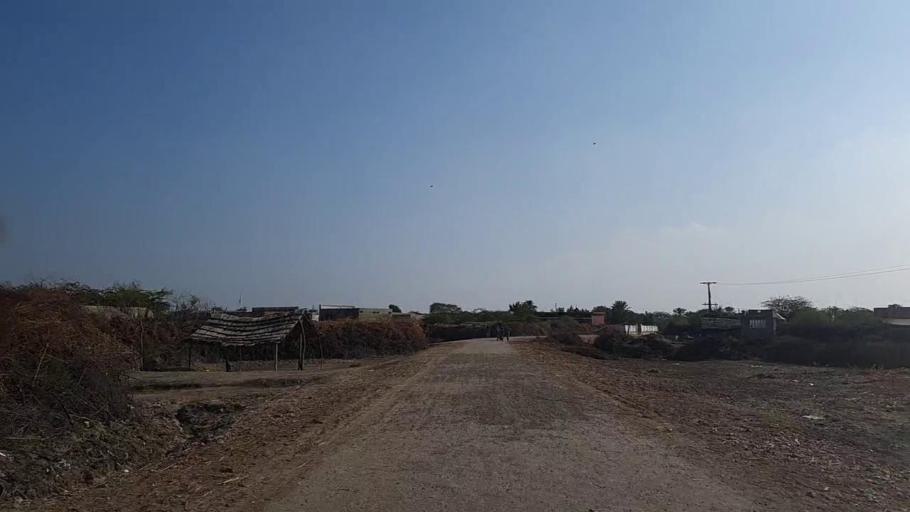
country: PK
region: Sindh
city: Jam Sahib
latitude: 26.2754
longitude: 68.5837
